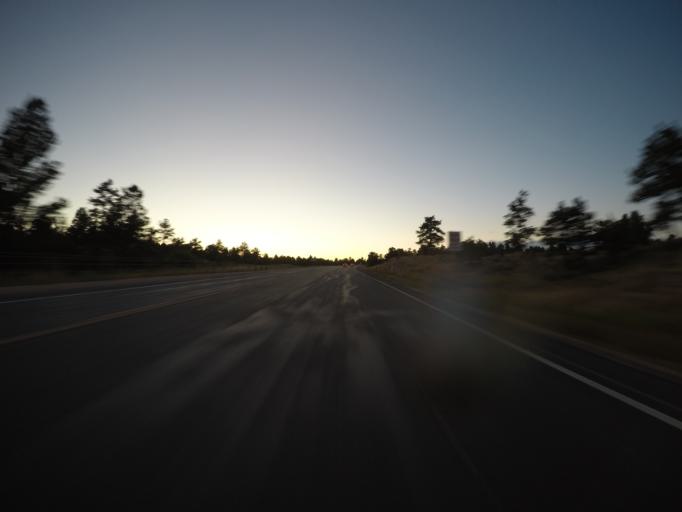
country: US
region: Wyoming
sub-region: Albany County
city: Laramie
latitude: 40.9888
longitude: -105.4078
